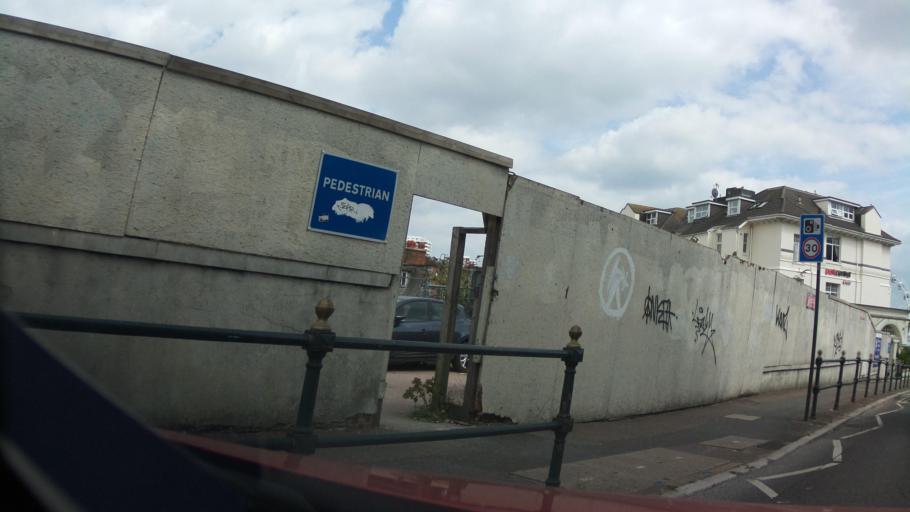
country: GB
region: England
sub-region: Bournemouth
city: Bournemouth
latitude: 50.7174
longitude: -1.8786
